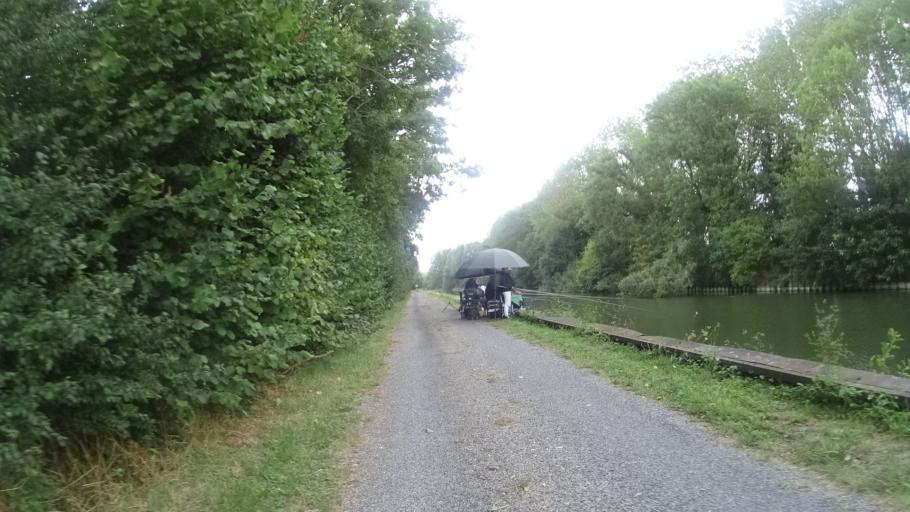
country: FR
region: Picardie
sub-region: Departement de l'Aisne
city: Ribemont
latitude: 49.8087
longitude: 3.4556
